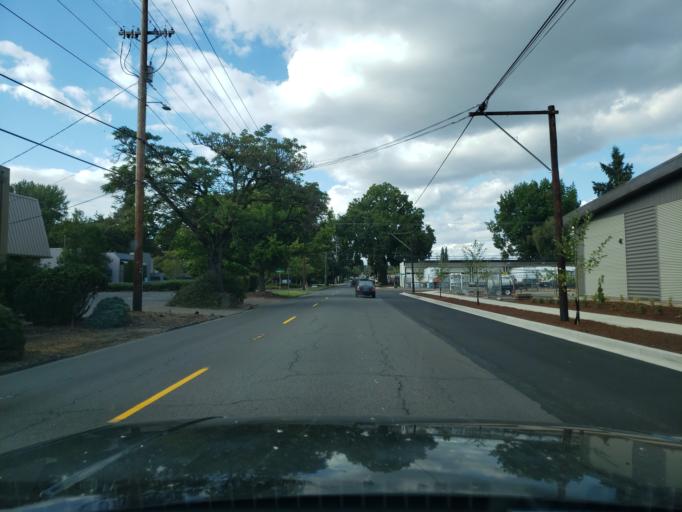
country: US
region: Oregon
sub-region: Marion County
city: Salem
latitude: 44.9625
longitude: -123.0341
